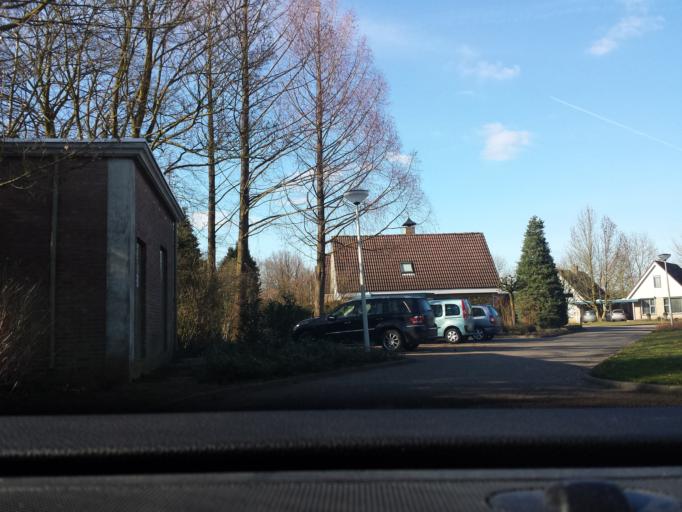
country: NL
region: Gelderland
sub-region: Gemeente Lochem
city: Almen
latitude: 52.1069
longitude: 6.3136
